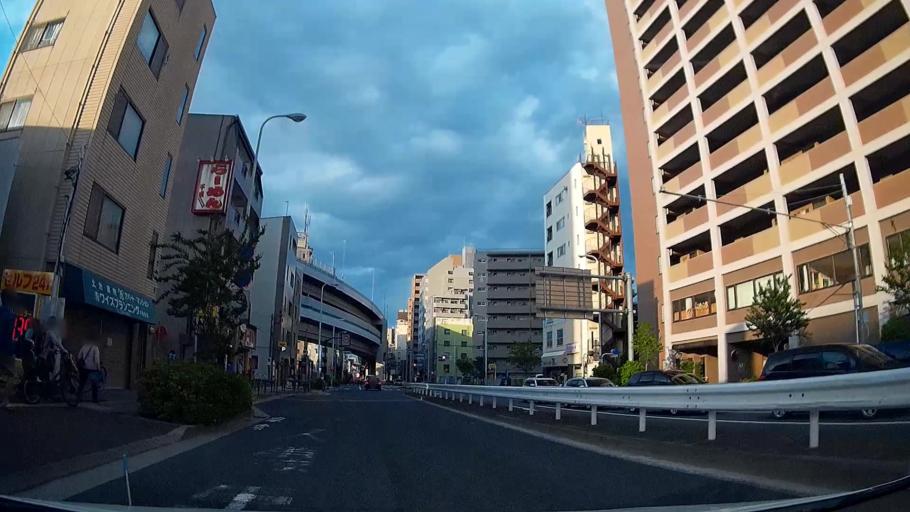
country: JP
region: Saitama
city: Kawaguchi
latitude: 35.7445
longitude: 139.7283
